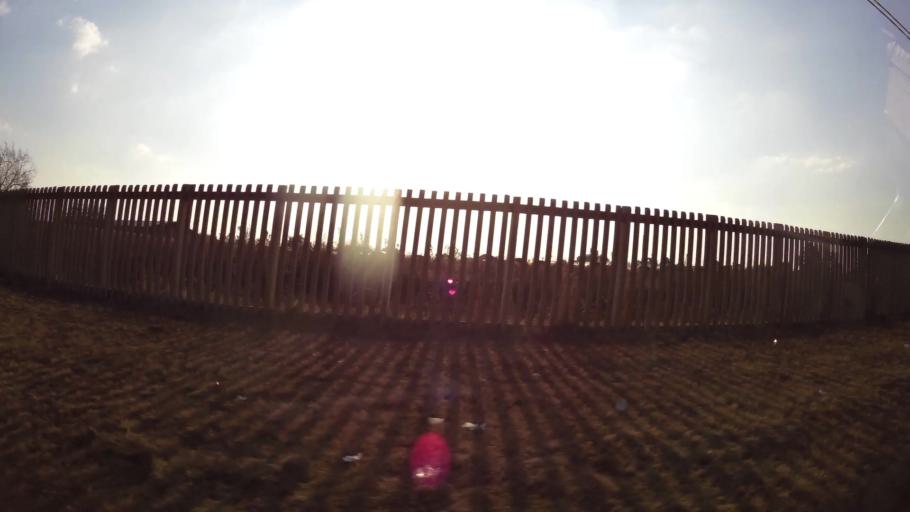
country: ZA
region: Gauteng
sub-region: Ekurhuleni Metropolitan Municipality
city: Benoni
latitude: -26.1444
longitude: 28.3706
